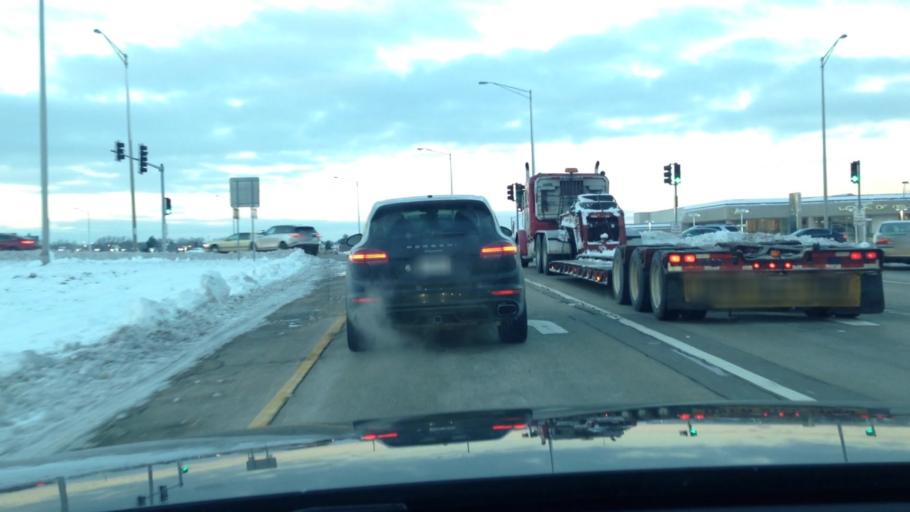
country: US
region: Illinois
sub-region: Lake County
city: Long Grove
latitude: 42.1386
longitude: -88.0026
